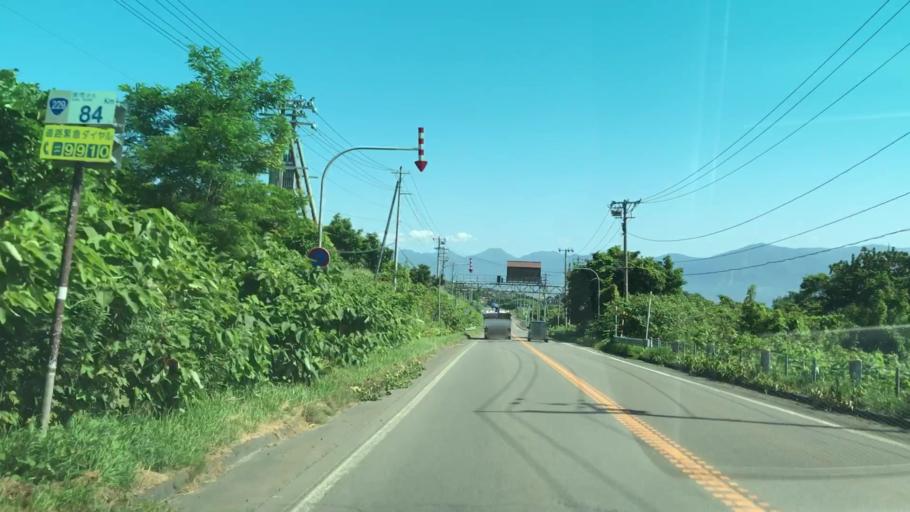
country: JP
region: Hokkaido
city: Iwanai
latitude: 43.0758
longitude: 140.4874
